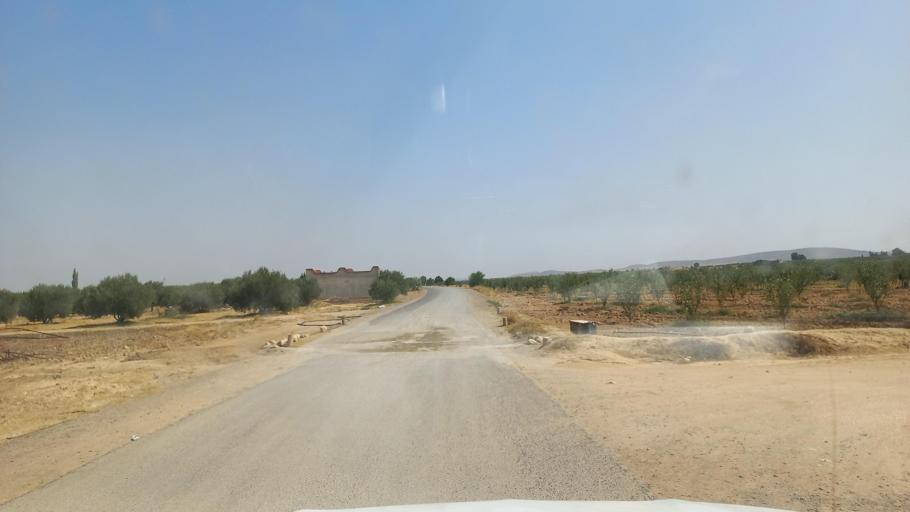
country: TN
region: Al Qasrayn
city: Kasserine
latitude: 35.2422
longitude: 9.0281
